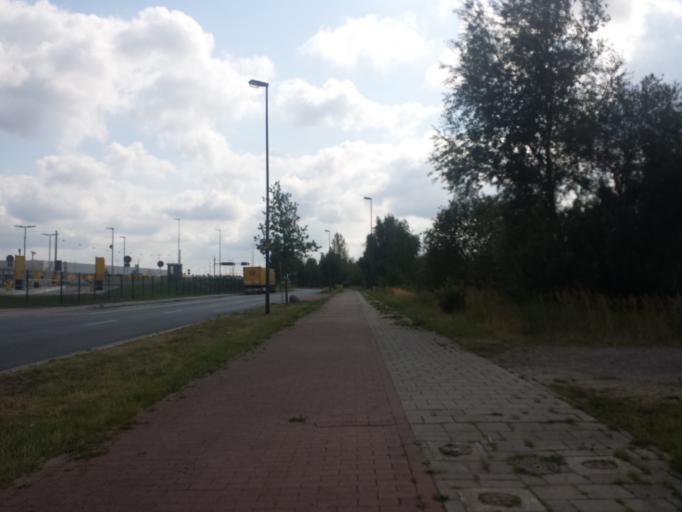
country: DE
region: Lower Saxony
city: Stuhr
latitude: 53.1012
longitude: 8.7050
